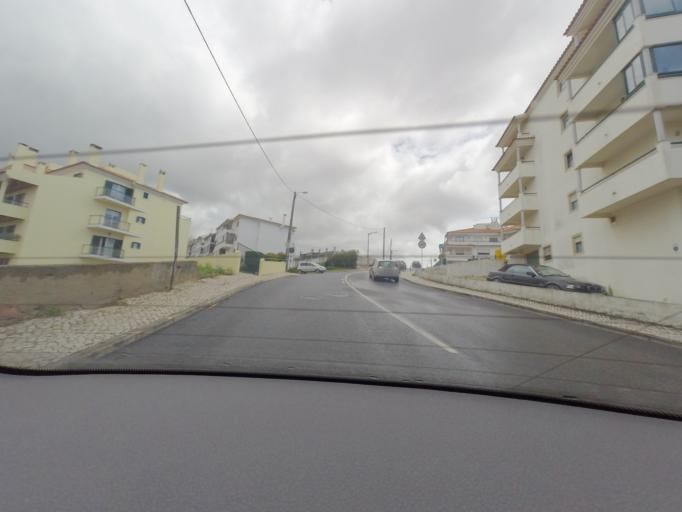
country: PT
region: Lisbon
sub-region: Cascais
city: Parede
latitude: 38.7113
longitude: -9.3651
